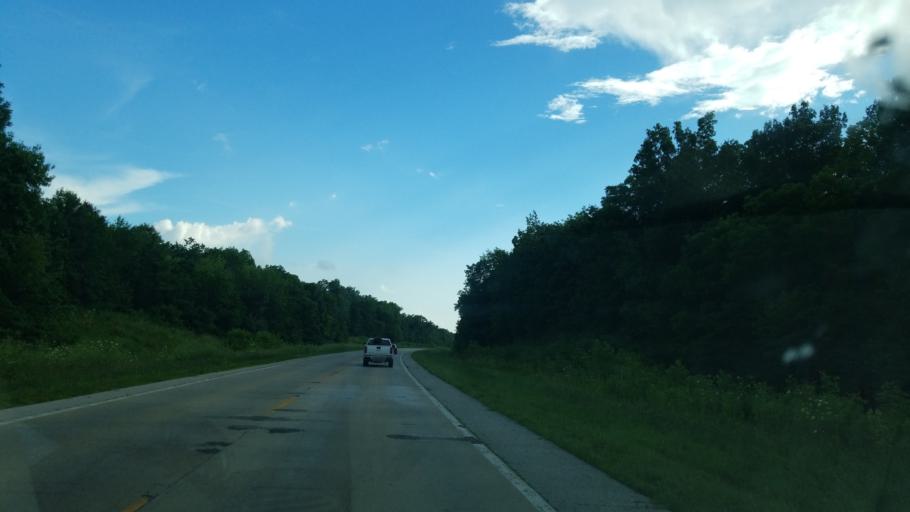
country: US
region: Illinois
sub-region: Marion County
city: Central City
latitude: 38.5704
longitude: -89.1114
